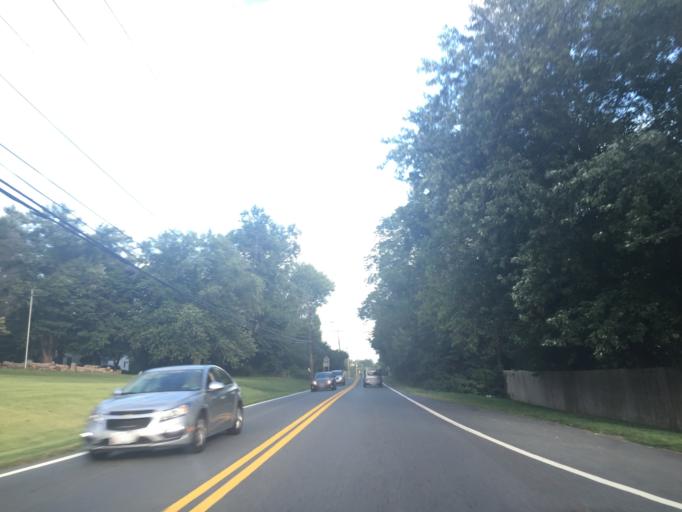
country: US
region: Maryland
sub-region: Montgomery County
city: Rossmoor
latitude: 39.1138
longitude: -77.0929
